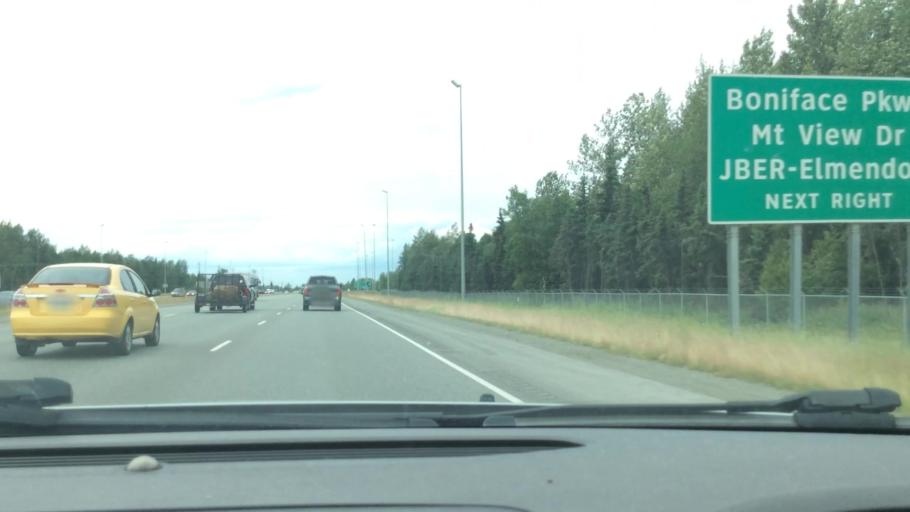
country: US
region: Alaska
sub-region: Anchorage Municipality
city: Elmendorf Air Force Base
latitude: 61.2247
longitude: -149.7611
